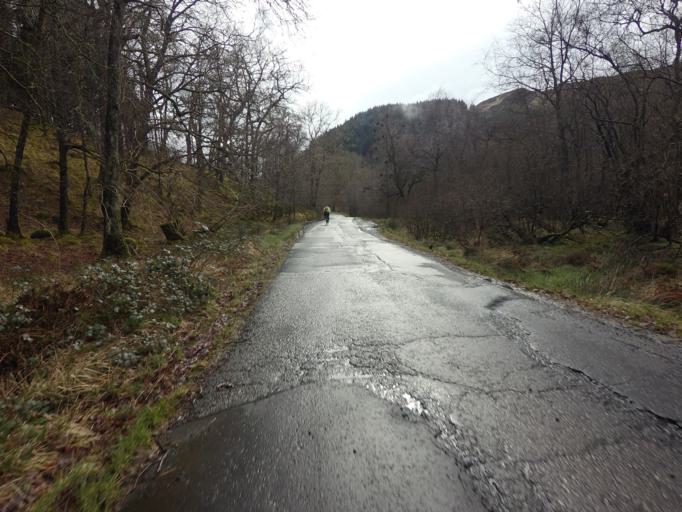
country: GB
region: Scotland
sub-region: West Dunbartonshire
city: Balloch
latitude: 56.2072
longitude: -4.5337
